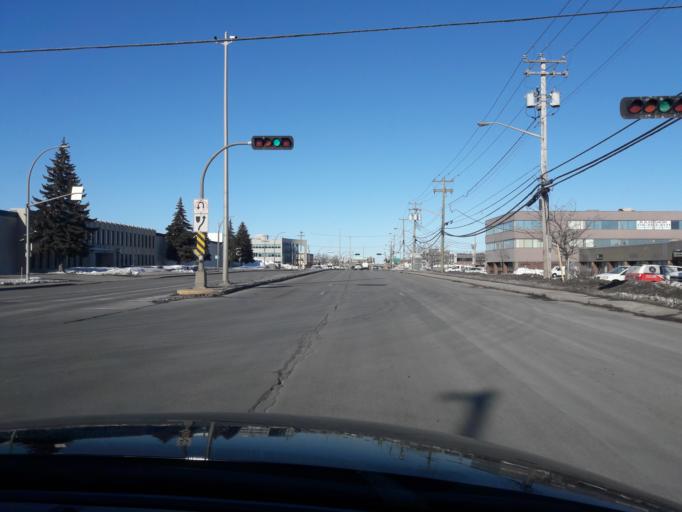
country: CA
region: Quebec
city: Dorval
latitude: 45.4851
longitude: -73.7195
